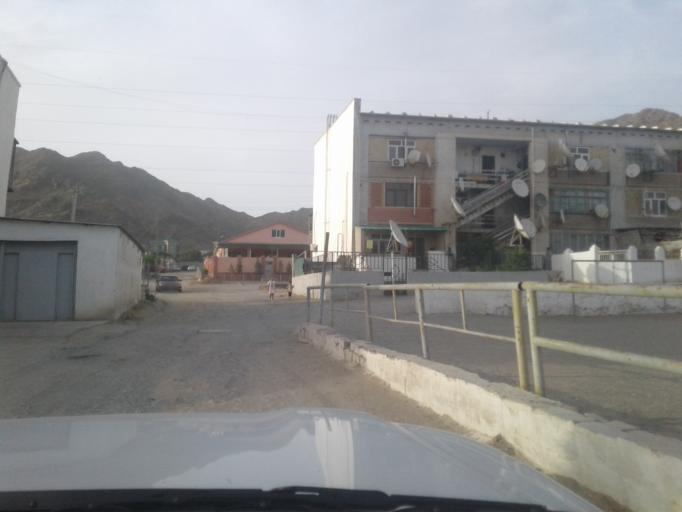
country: TM
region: Balkan
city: Turkmenbasy
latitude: 40.0056
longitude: 52.9650
